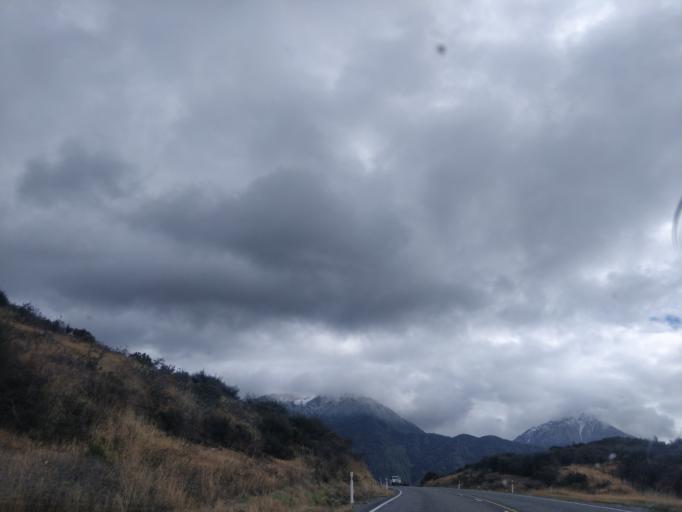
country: NZ
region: Canterbury
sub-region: Waimakariri District
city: Oxford
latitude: -43.0157
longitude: 171.7461
